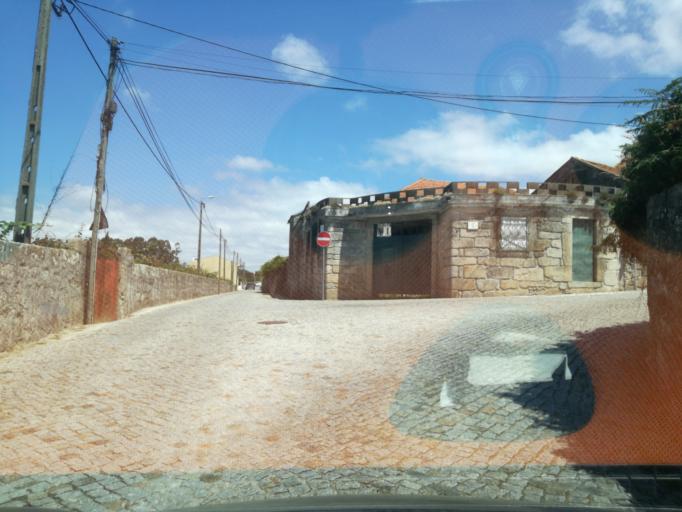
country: PT
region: Porto
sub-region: Maia
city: Maia
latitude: 41.2442
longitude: -8.6084
